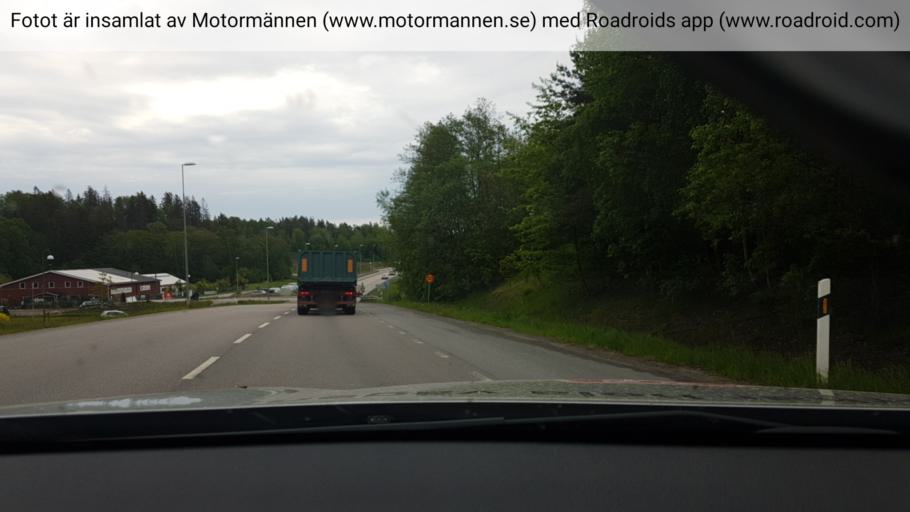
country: SE
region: Stockholm
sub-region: Nynashamns Kommun
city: Osmo
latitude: 58.9792
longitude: 17.9046
